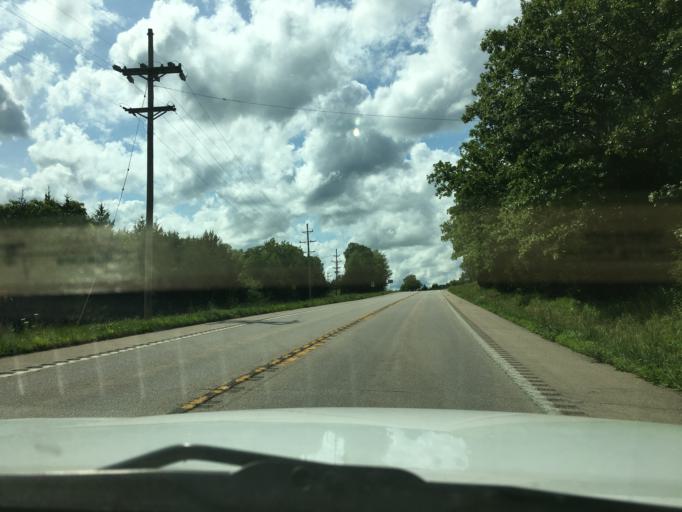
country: US
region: Missouri
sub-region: Franklin County
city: Gerald
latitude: 38.4217
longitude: -91.2584
